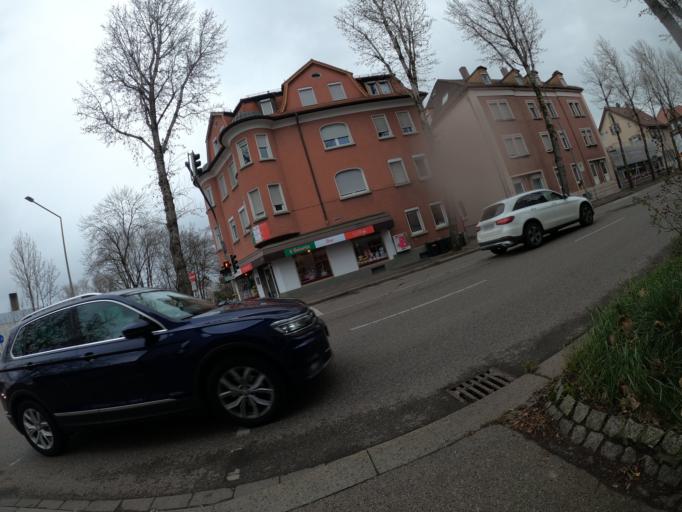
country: DE
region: Baden-Wuerttemberg
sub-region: Regierungsbezirk Stuttgart
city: Goeppingen
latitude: 48.6993
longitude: 9.6634
